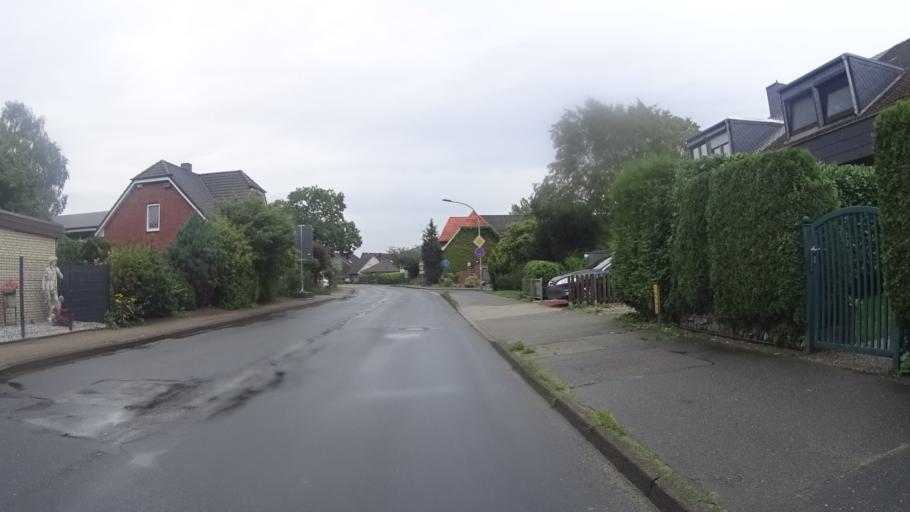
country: DE
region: Schleswig-Holstein
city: Alveslohe
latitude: 53.7867
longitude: 9.9160
